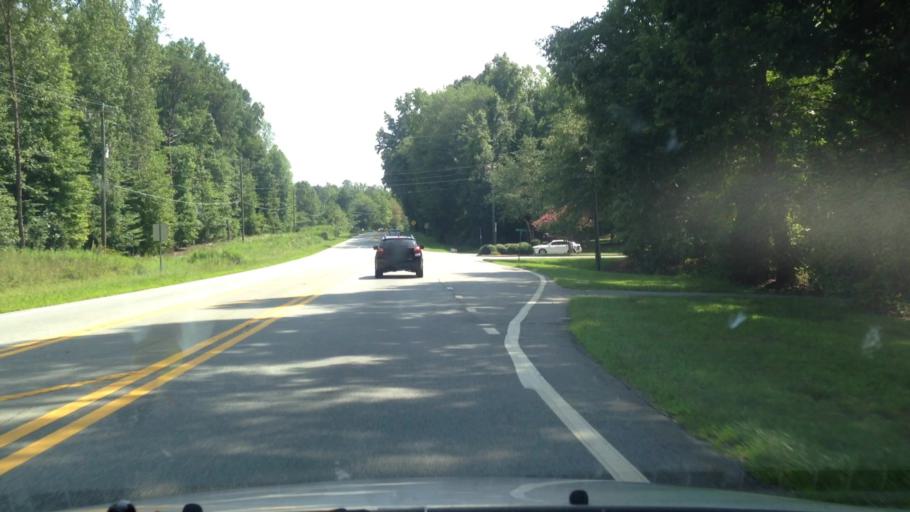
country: US
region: North Carolina
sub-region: Guilford County
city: Oak Ridge
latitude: 36.1878
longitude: -79.9860
